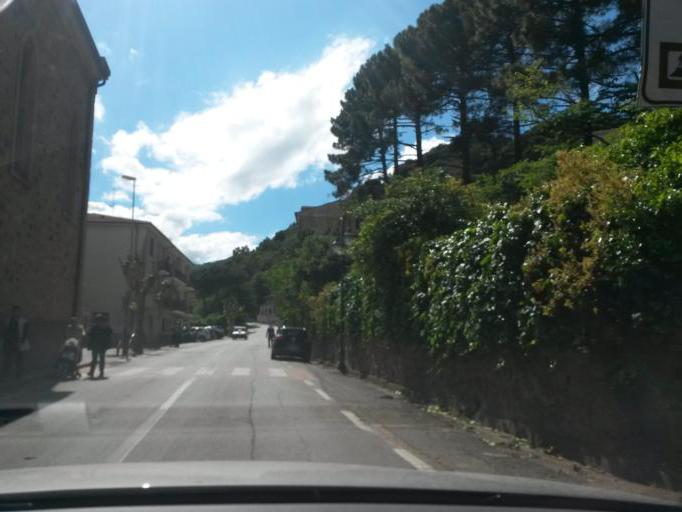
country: IT
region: Tuscany
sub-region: Provincia di Livorno
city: Rio Marina
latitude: 42.8144
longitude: 10.4232
